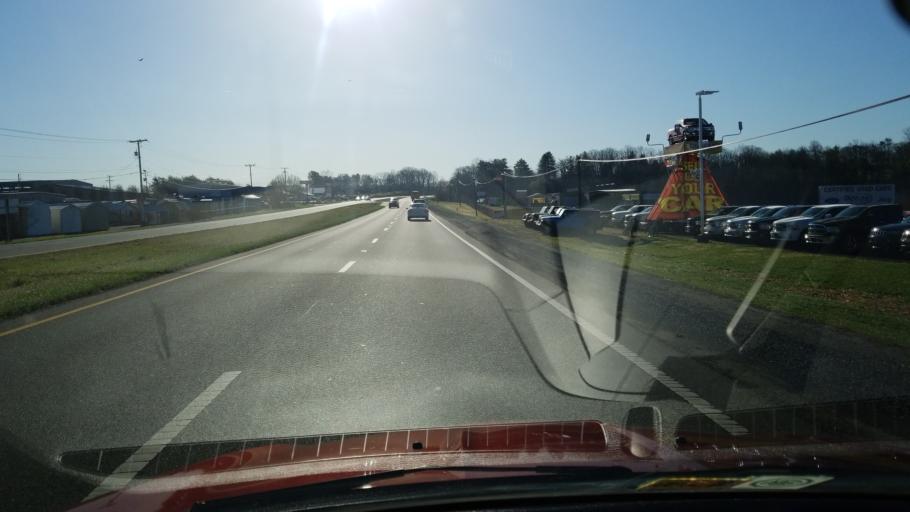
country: US
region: Virginia
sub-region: Franklin County
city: Rocky Mount
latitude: 37.0691
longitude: -79.8926
